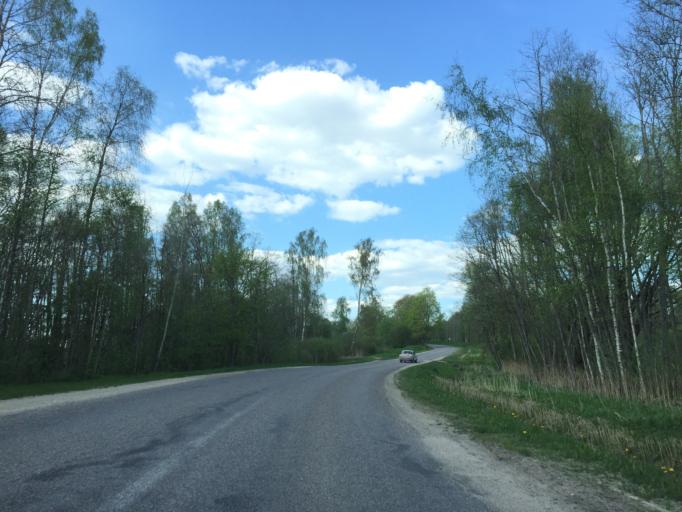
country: LV
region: Limbazu Rajons
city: Limbazi
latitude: 57.4751
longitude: 24.7107
